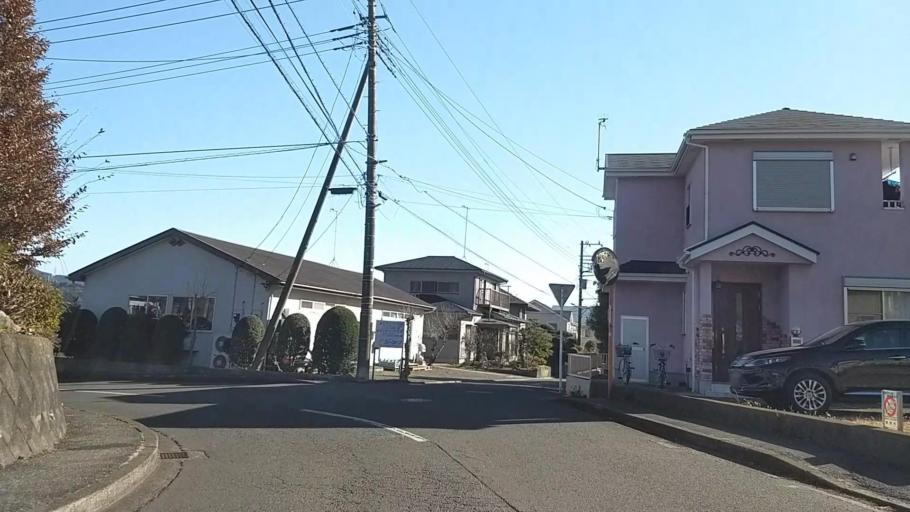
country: JP
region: Kanagawa
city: Hadano
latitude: 35.3925
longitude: 139.1931
